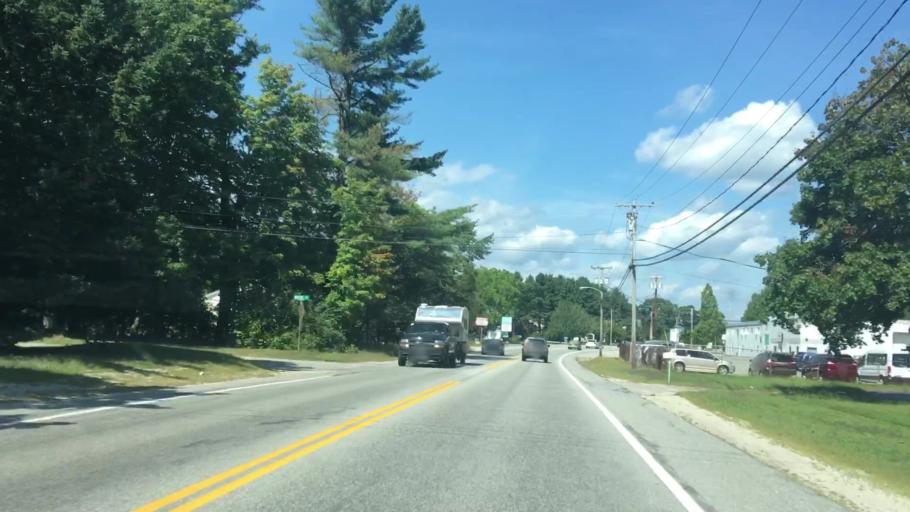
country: US
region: Maine
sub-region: Cumberland County
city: New Gloucester
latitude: 43.8938
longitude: -70.3280
